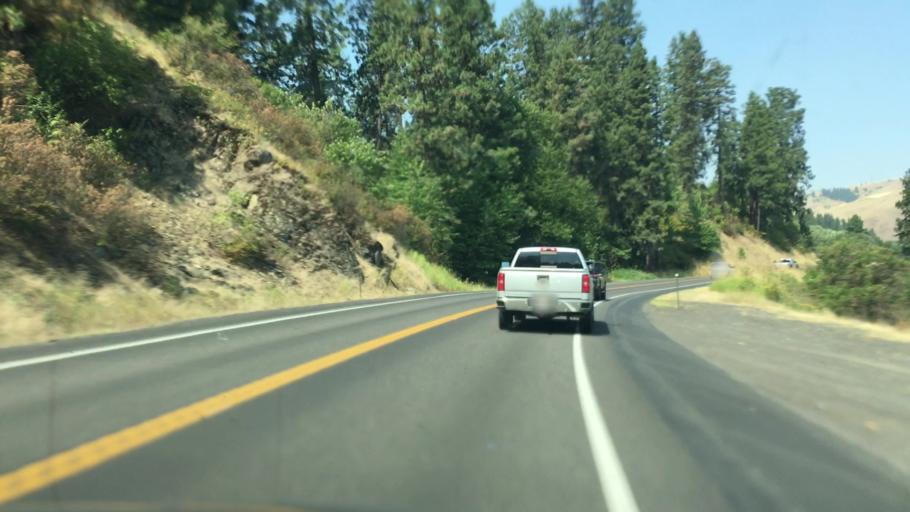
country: US
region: Idaho
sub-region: Clearwater County
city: Orofino
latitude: 46.5003
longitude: -116.5002
